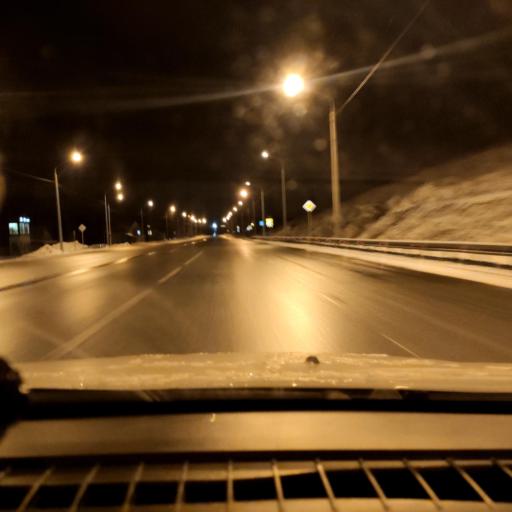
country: RU
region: Samara
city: Volzhskiy
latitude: 53.4375
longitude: 50.1113
